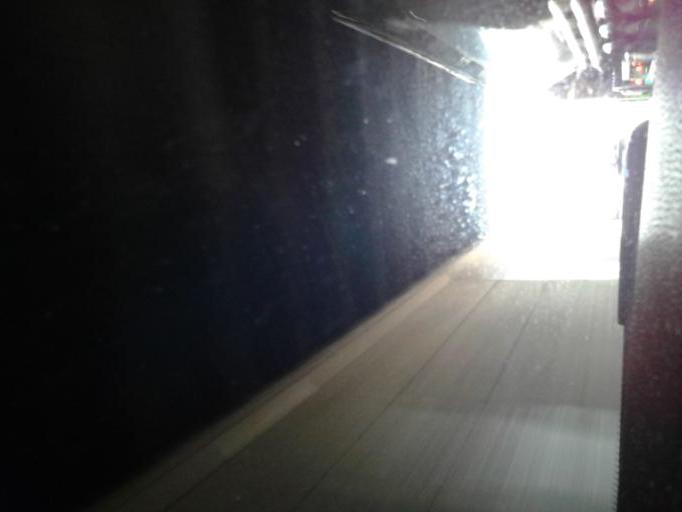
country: FR
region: Aquitaine
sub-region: Departement des Pyrenees-Atlantiques
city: Guethary
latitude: 43.4173
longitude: -1.6045
